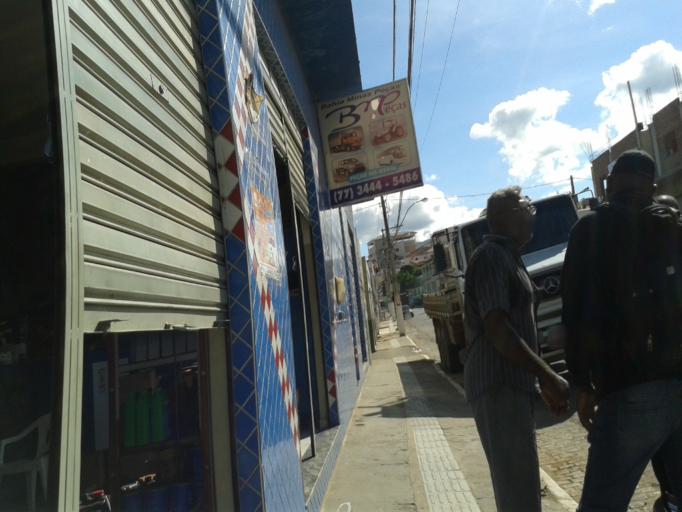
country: BR
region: Bahia
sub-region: Livramento Do Brumado
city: Livramento do Brumado
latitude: -13.6539
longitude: -41.8427
